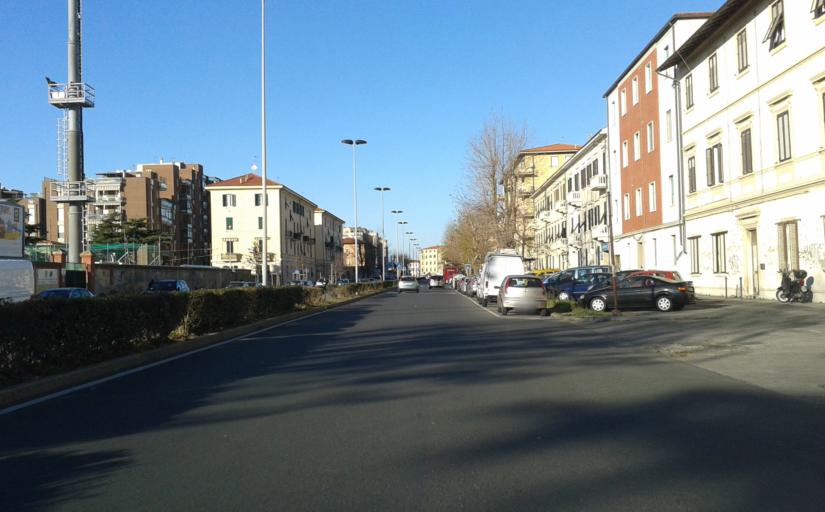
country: IT
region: Tuscany
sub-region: Provincia di Livorno
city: Livorno
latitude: 43.5551
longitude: 10.3272
